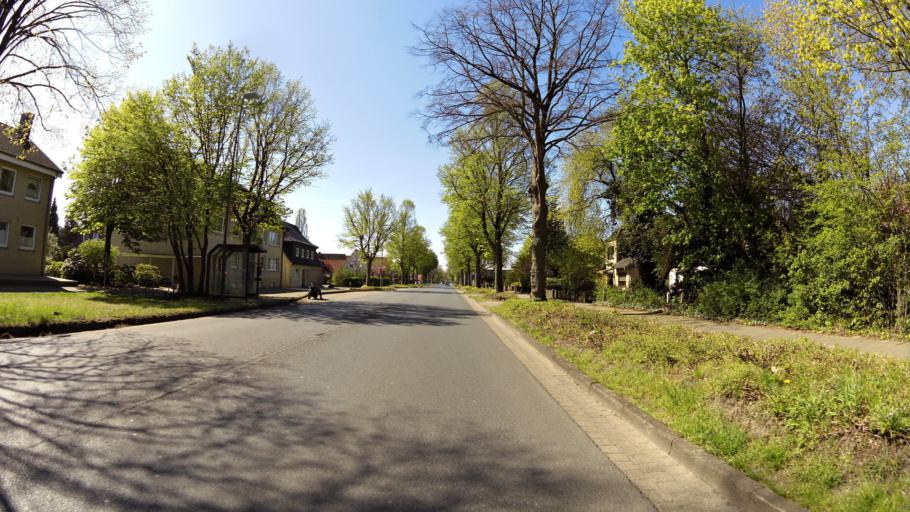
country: DE
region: Lower Saxony
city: Rotenburg
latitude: 53.1182
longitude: 9.4209
